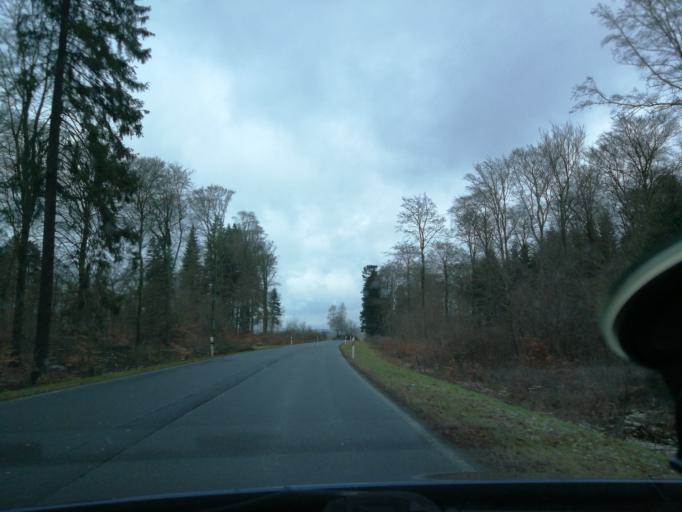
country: DE
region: Rheinland-Pfalz
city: Dreis-Bruck
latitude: 50.2538
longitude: 6.8074
